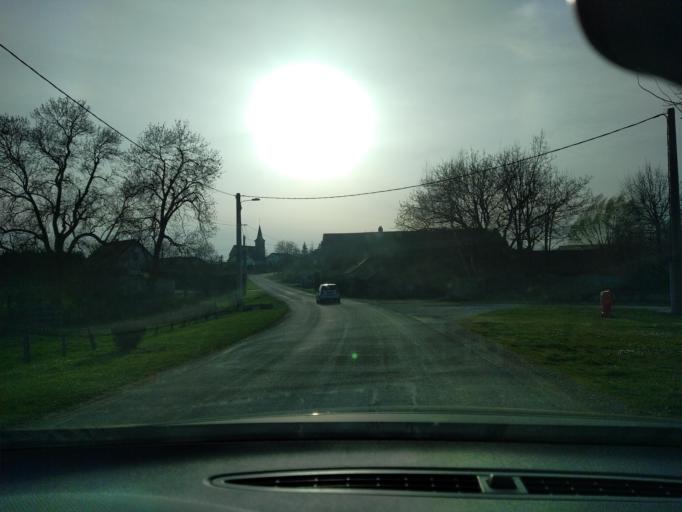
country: FR
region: Franche-Comte
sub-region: Departement du Jura
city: Chaussin
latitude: 46.9827
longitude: 5.4339
